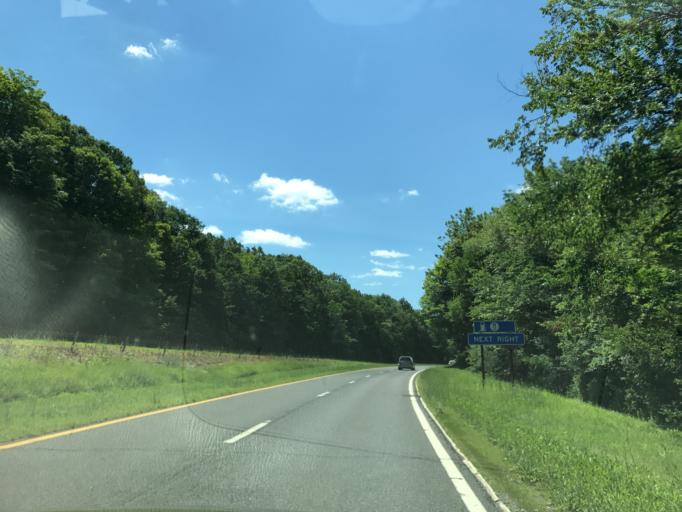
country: US
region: New York
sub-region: Dutchess County
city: Pleasant Valley
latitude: 41.7899
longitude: -73.7704
